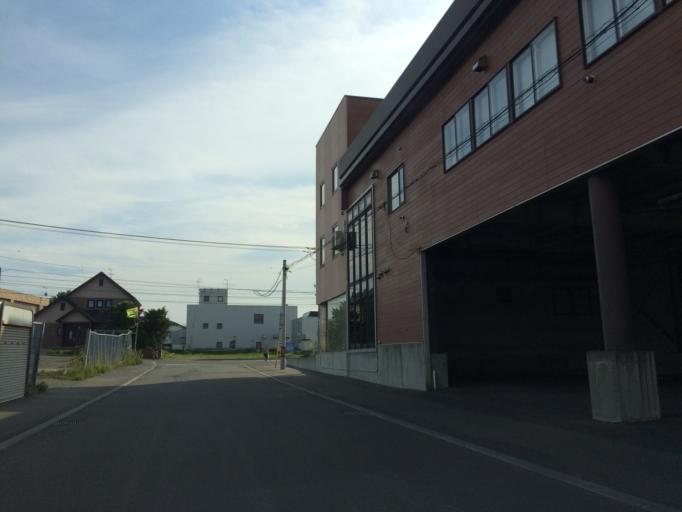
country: JP
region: Hokkaido
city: Ebetsu
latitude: 43.1119
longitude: 141.5490
